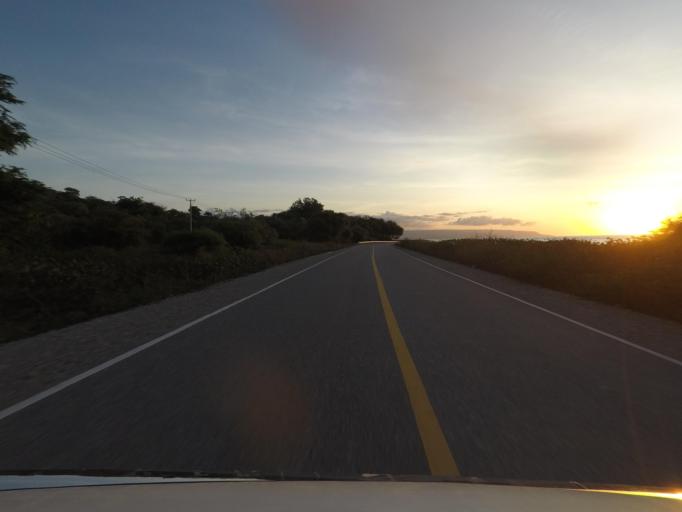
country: TL
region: Baucau
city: Baucau
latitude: -8.4587
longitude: 126.6139
